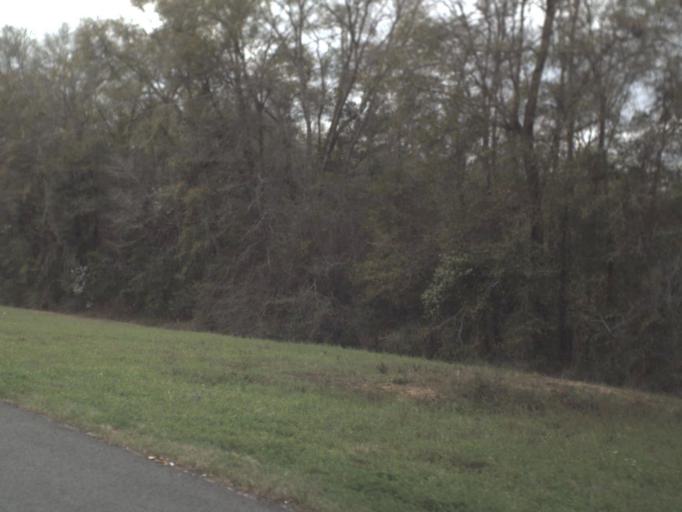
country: US
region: Florida
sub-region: Gadsden County
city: Quincy
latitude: 30.4767
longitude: -84.6277
